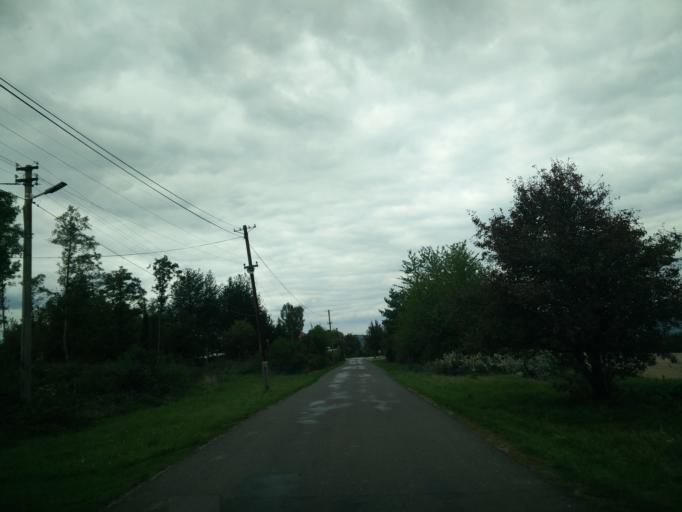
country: SK
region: Nitriansky
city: Novaky
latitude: 48.6109
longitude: 18.5047
